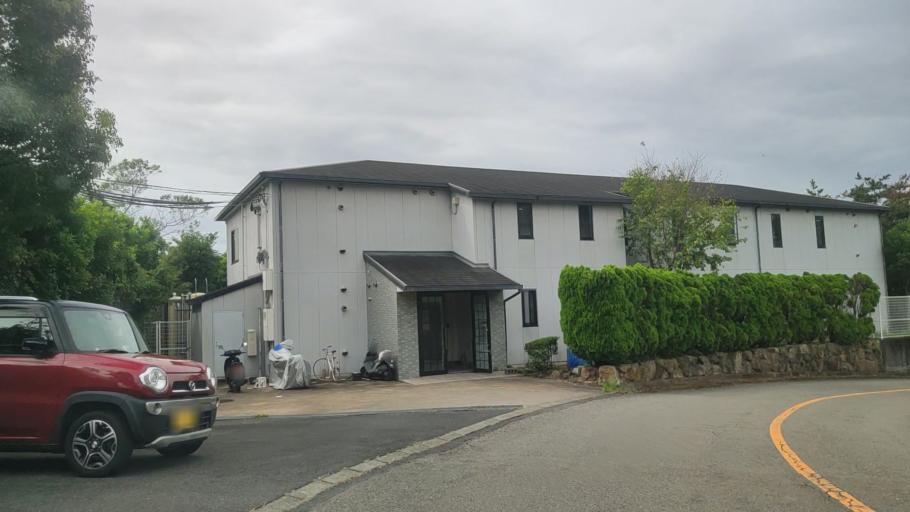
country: JP
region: Wakayama
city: Tanabe
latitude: 33.6673
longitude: 135.3700
